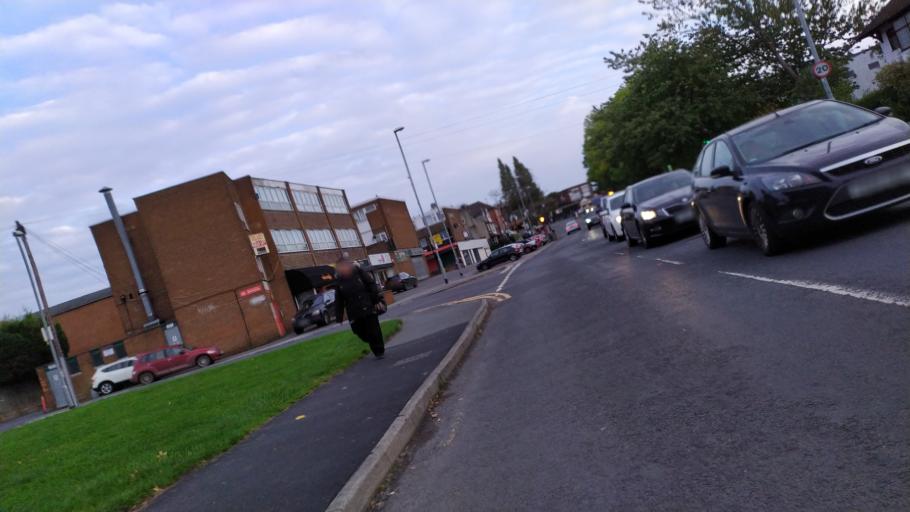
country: GB
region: England
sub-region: City and Borough of Leeds
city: Chapel Allerton
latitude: 53.8295
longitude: -1.5680
